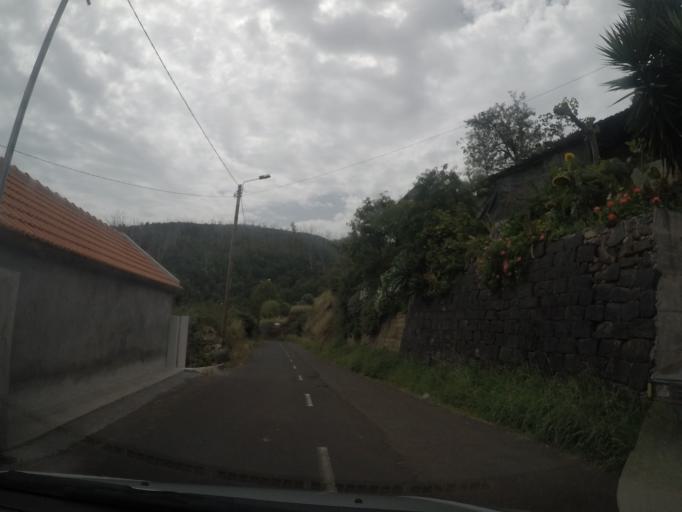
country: PT
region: Madeira
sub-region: Santa Cruz
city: Santa Cruz
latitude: 32.6821
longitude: -16.8091
